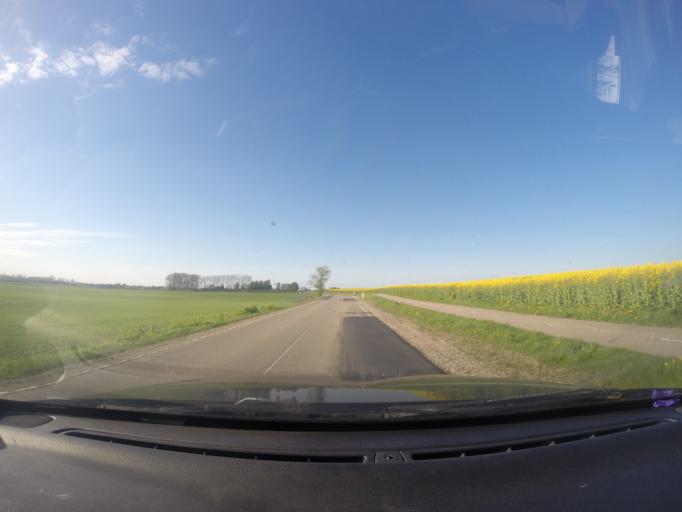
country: DK
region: Capital Region
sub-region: Hoje-Taastrup Kommune
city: Taastrup
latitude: 55.6731
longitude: 12.2539
